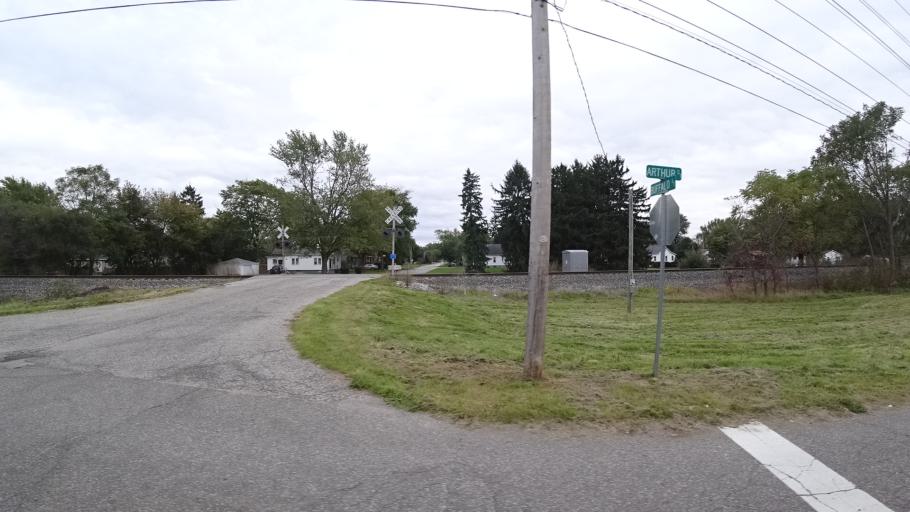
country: US
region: Indiana
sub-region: LaPorte County
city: Michigan City
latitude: 41.7004
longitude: -86.9006
